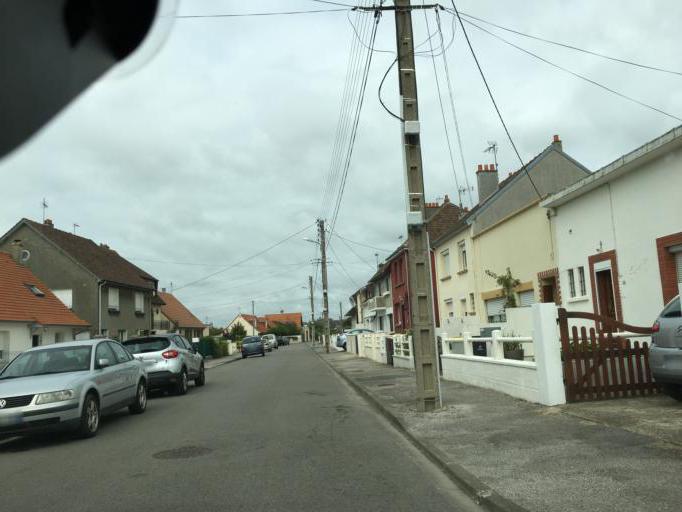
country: FR
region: Nord-Pas-de-Calais
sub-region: Departement du Pas-de-Calais
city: Berck
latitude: 50.4051
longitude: 1.5865
